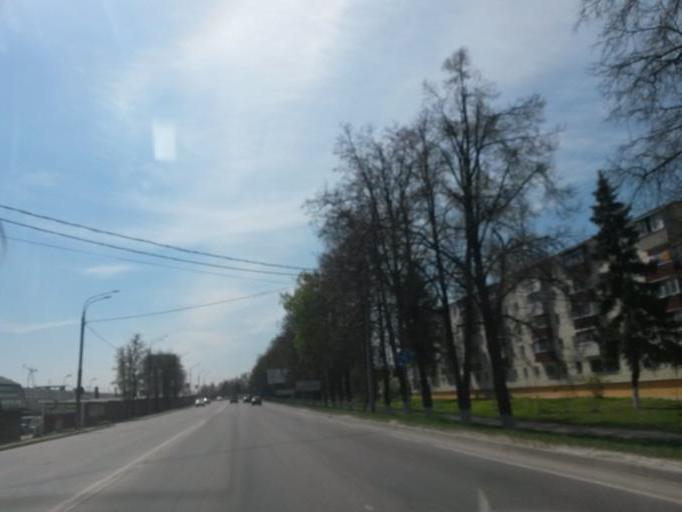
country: RU
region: Moskovskaya
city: Klimovsk
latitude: 55.3886
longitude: 37.5407
